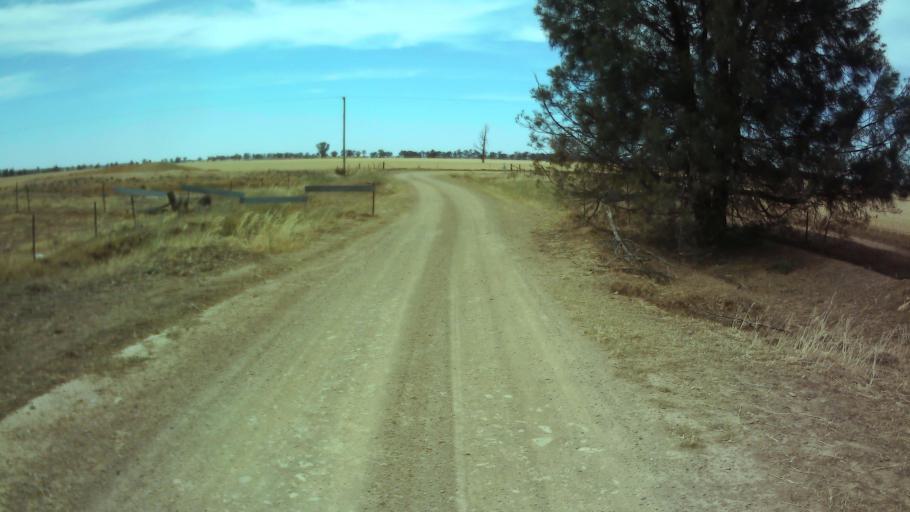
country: AU
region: New South Wales
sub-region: Weddin
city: Grenfell
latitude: -33.9425
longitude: 147.7793
